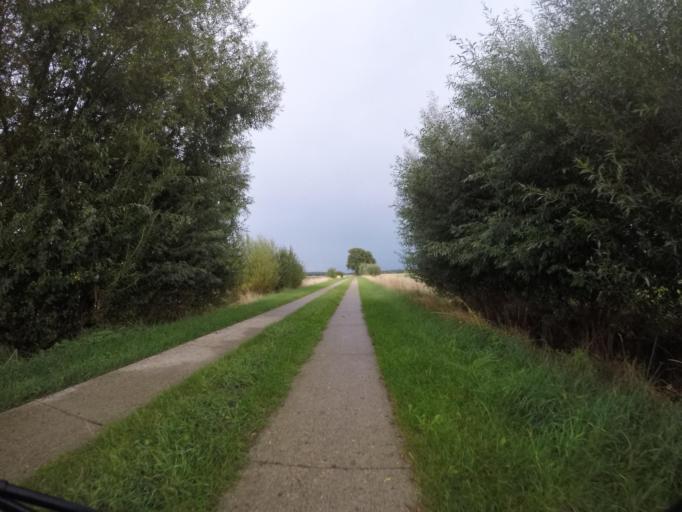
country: DE
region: Lower Saxony
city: Neu Darchau
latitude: 53.2577
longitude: 10.8871
